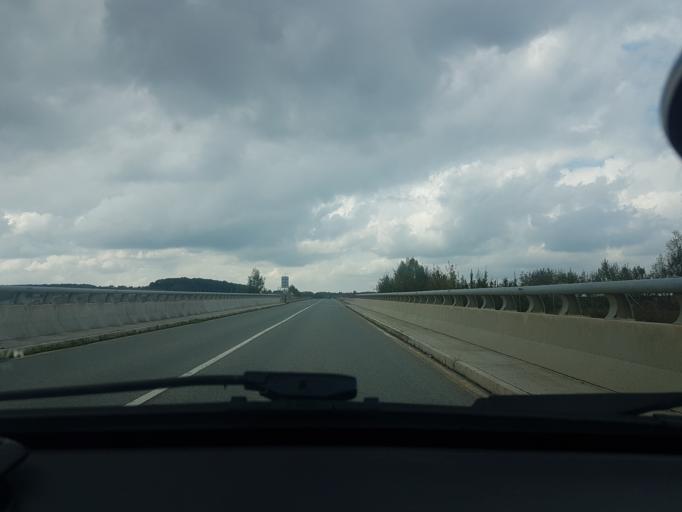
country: FR
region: Franche-Comte
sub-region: Departement de la Haute-Saone
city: Villersexel
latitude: 47.5445
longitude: 6.4805
